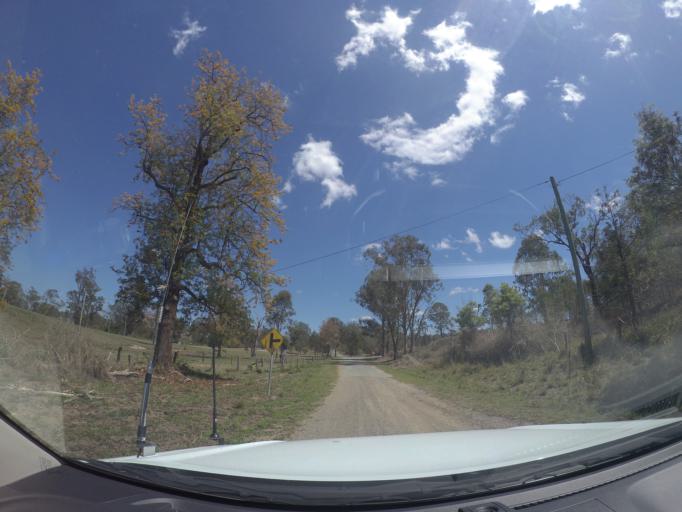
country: AU
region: Queensland
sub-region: Logan
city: Cedar Vale
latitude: -27.8507
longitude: 152.8953
